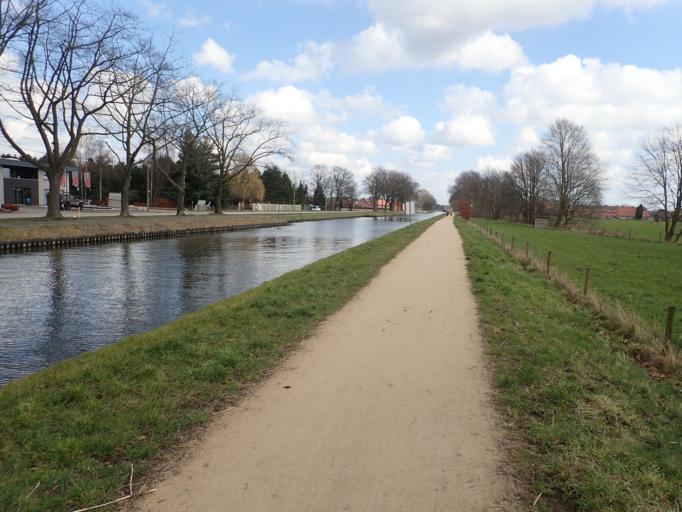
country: BE
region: Flanders
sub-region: Provincie Antwerpen
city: Beerse
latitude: 51.3276
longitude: 4.8561
